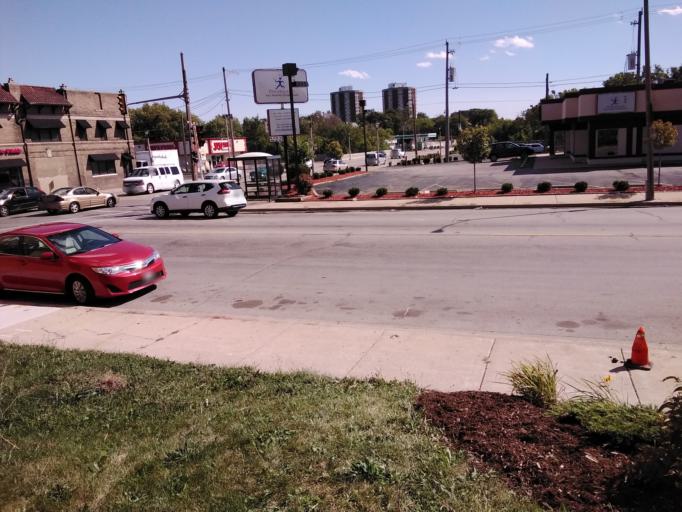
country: US
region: Wisconsin
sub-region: Milwaukee County
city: West Milwaukee
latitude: 43.0489
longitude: -87.9580
